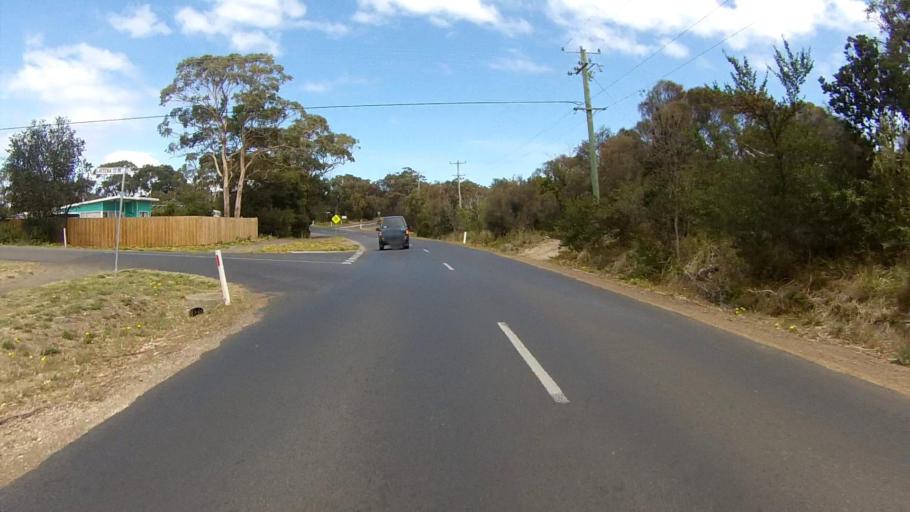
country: AU
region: Tasmania
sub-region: Sorell
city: Sorell
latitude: -42.8645
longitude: 147.6117
